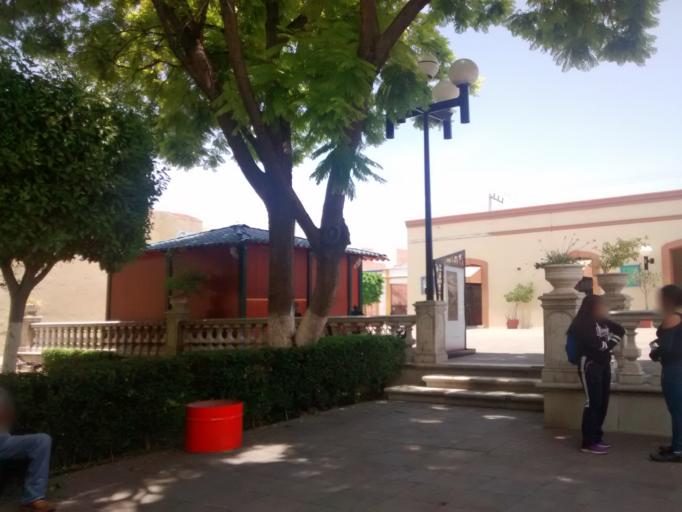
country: MX
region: Puebla
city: Tehuacan
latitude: 18.4664
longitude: -97.3936
